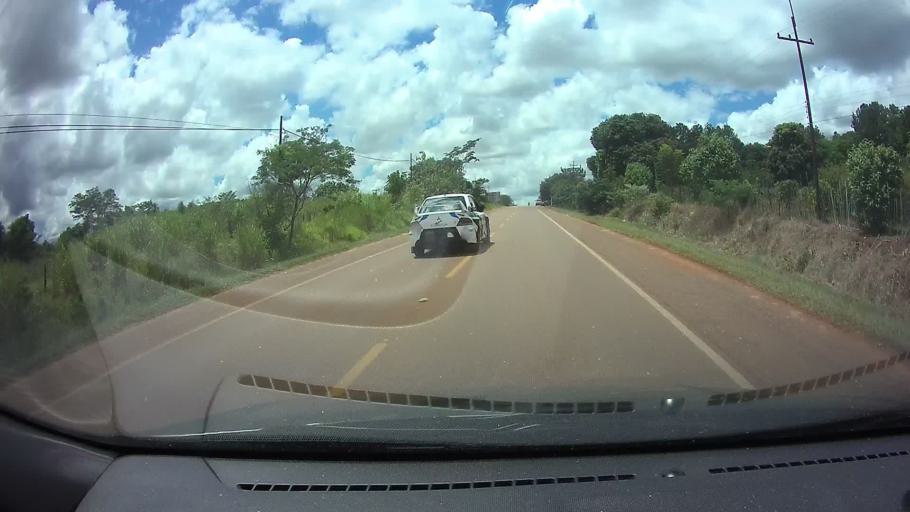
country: PY
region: Paraguari
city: La Colmena
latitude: -25.8915
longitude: -56.8260
